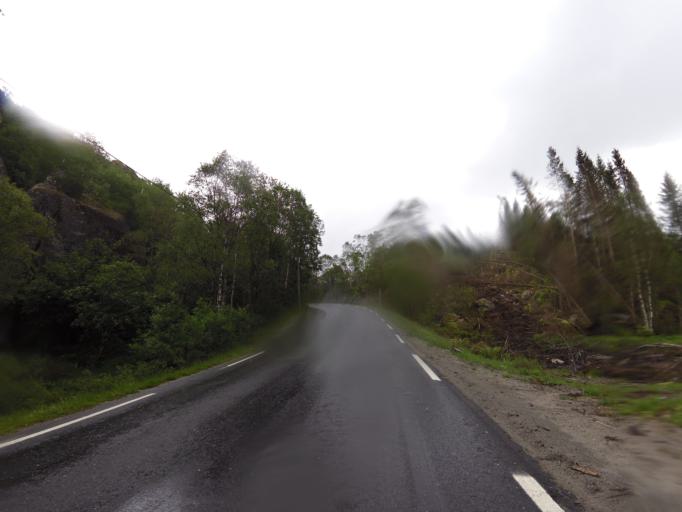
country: NO
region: Vest-Agder
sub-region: Lyngdal
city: Lyngdal
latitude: 58.1117
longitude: 7.0839
